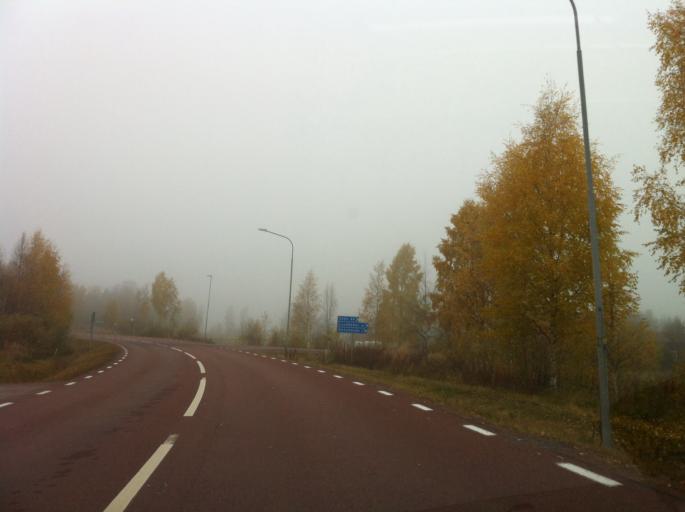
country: NO
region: Hedmark
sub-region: Trysil
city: Innbygda
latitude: 61.6887
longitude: 13.1625
